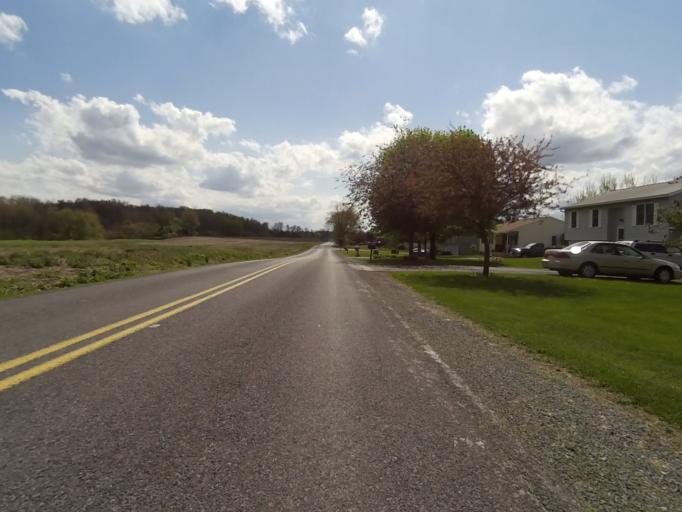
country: US
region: Pennsylvania
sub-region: Centre County
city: Bellefonte
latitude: 40.8814
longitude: -77.8205
